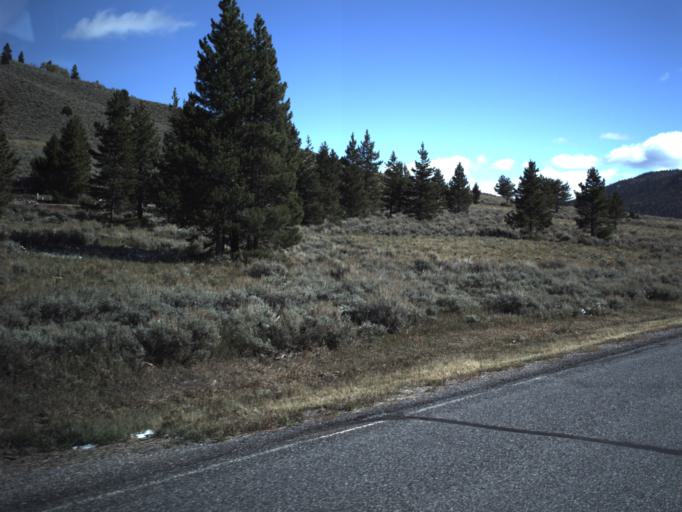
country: US
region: Utah
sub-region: Wayne County
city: Loa
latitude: 38.5630
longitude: -111.7038
